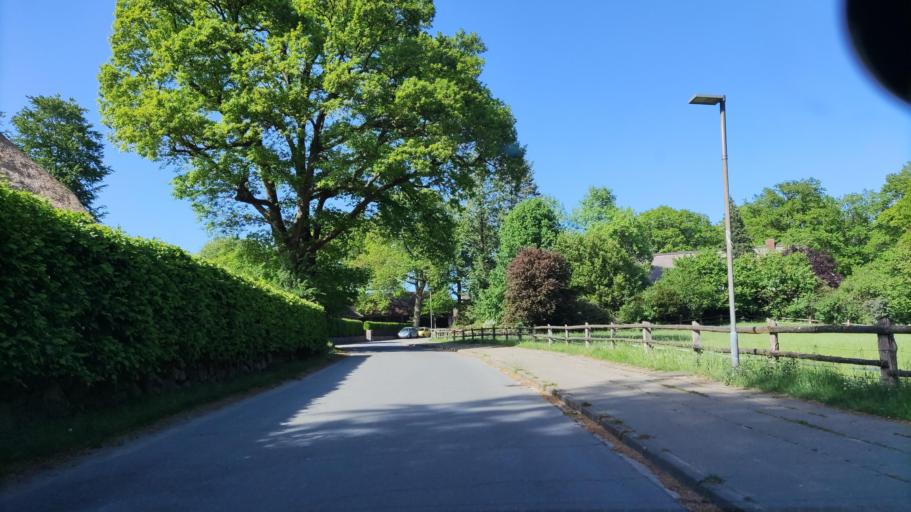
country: DE
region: Lower Saxony
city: Undeloh
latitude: 53.1446
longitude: 9.9217
